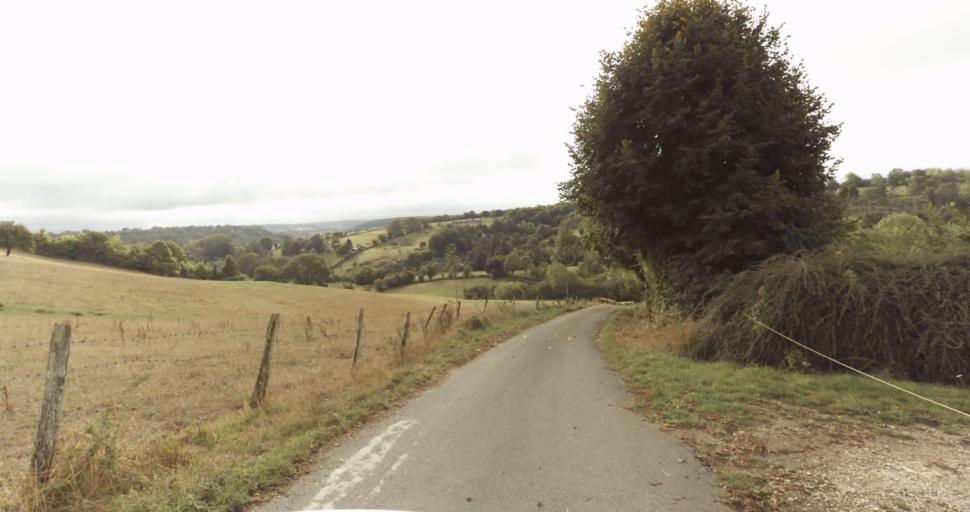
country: FR
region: Lower Normandy
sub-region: Departement de l'Orne
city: Vimoutiers
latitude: 48.9240
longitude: 0.1693
